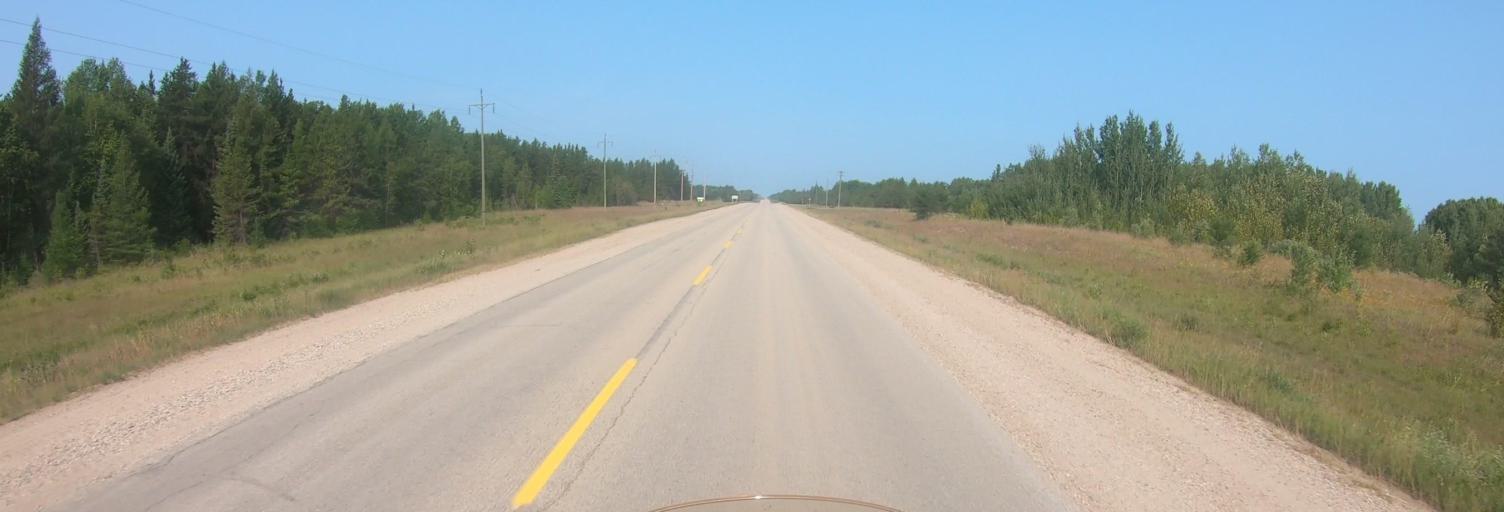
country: US
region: Minnesota
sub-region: Roseau County
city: Roseau
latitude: 49.0391
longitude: -95.7738
